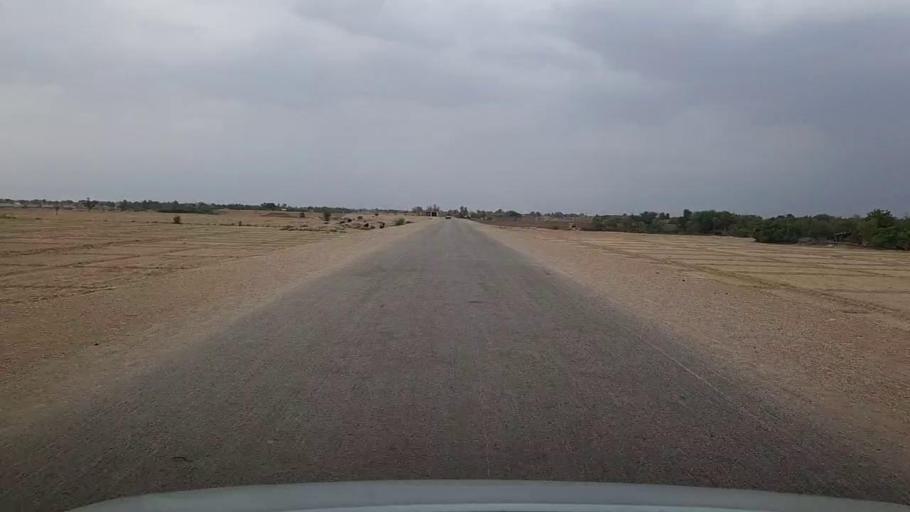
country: PK
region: Sindh
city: Sehwan
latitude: 26.3430
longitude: 67.7263
